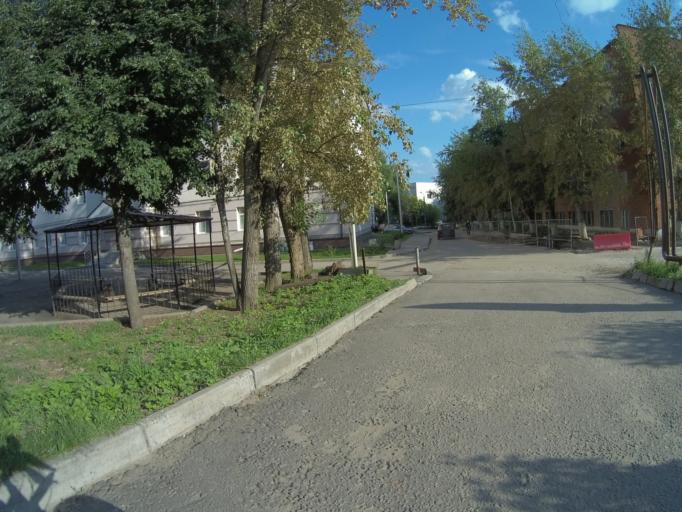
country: RU
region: Vladimir
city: Vladimir
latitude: 56.1421
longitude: 40.3829
